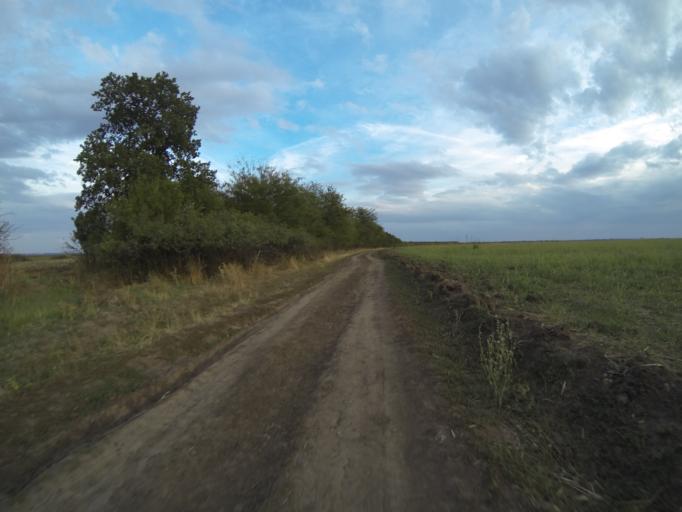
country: RO
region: Dolj
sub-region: Comuna Ceratu
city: Ceratu
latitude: 44.0939
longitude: 23.6717
